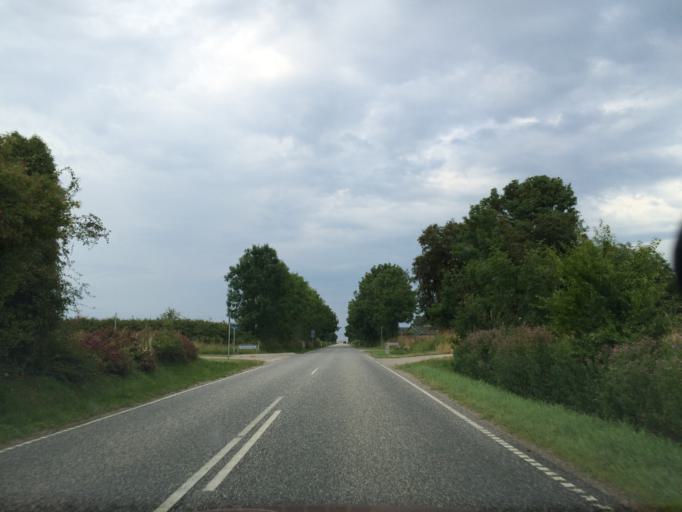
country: DK
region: South Denmark
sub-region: Sonderborg Kommune
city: Broager
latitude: 54.9274
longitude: 9.6867
